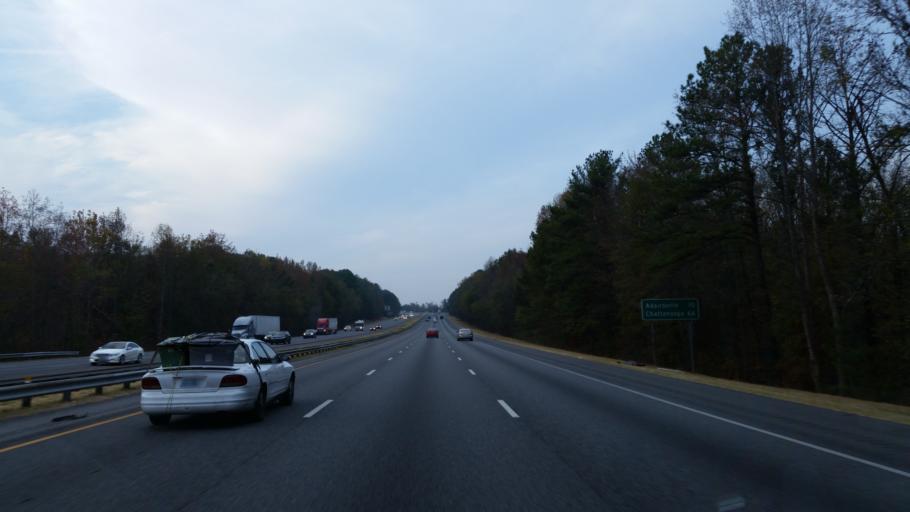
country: US
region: Georgia
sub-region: Bartow County
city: Rydal
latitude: 34.2848
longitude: -84.8202
